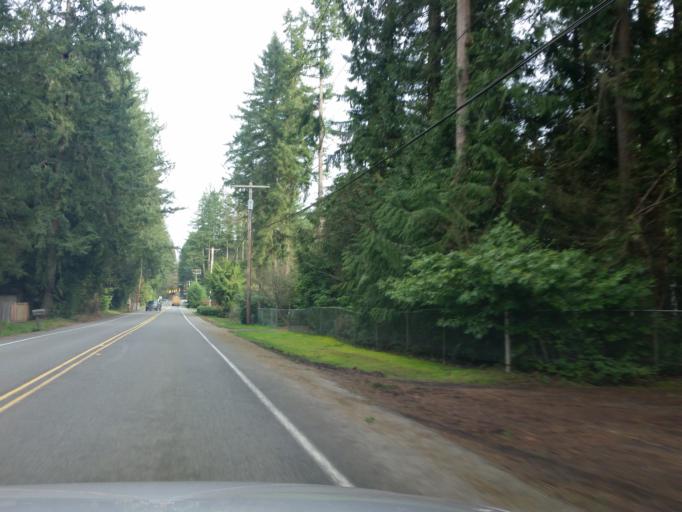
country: US
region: Washington
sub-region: King County
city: Cottage Lake
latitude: 47.7473
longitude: -122.0875
